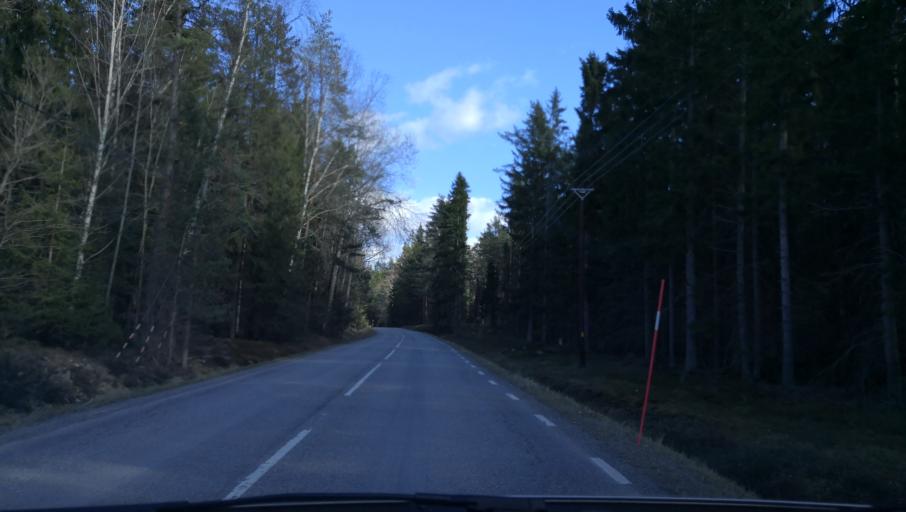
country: SE
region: Stockholm
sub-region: Varmdo Kommun
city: Hemmesta
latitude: 59.3568
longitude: 18.5663
